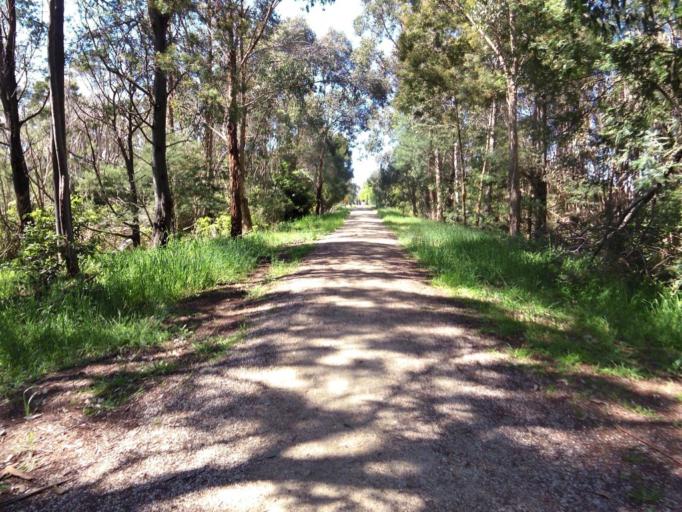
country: AU
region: Victoria
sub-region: Latrobe
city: Morwell
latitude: -38.6663
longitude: 146.3175
